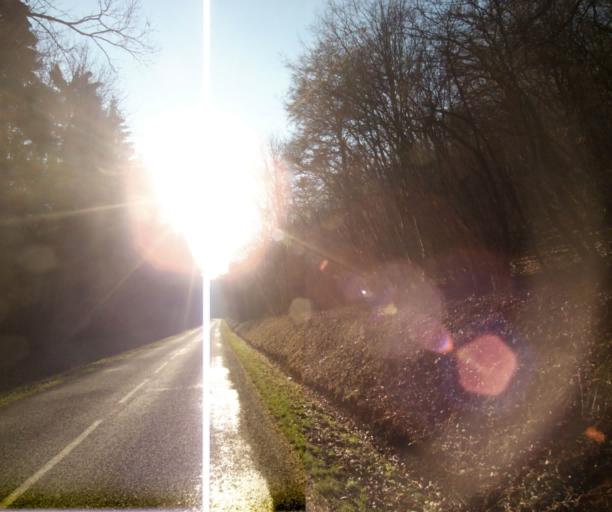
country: FR
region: Champagne-Ardenne
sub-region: Departement de la Haute-Marne
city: Chevillon
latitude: 48.5334
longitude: 5.1839
